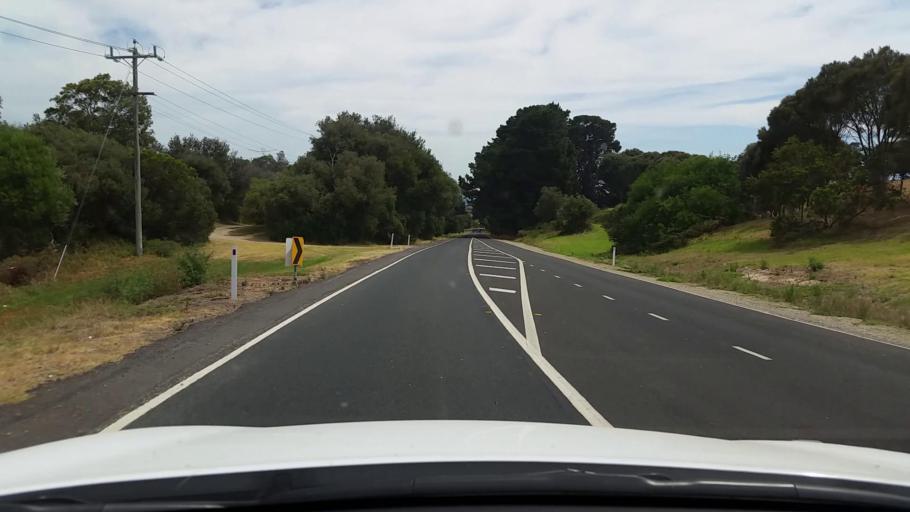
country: AU
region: Victoria
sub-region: Mornington Peninsula
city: Saint Andrews Beach
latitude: -38.4553
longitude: 144.8989
